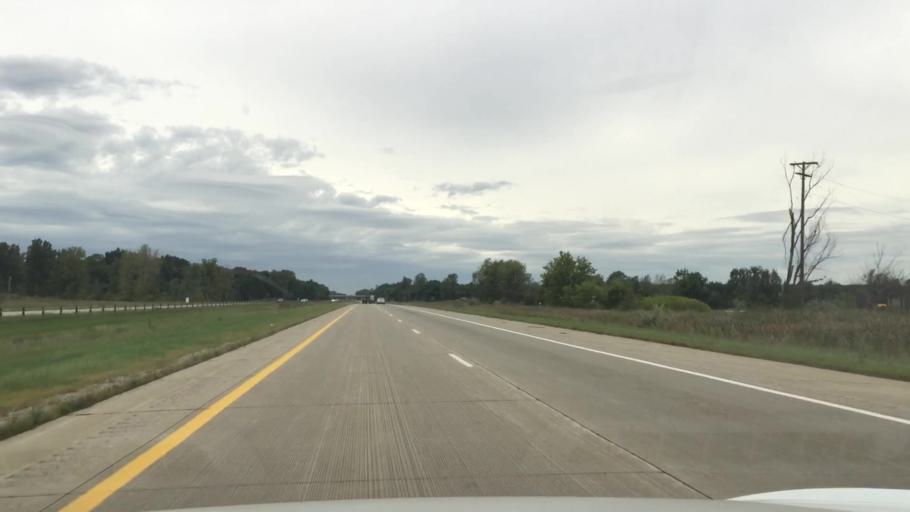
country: US
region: Michigan
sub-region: Saint Clair County
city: Saint Clair
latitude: 42.8444
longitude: -82.5833
